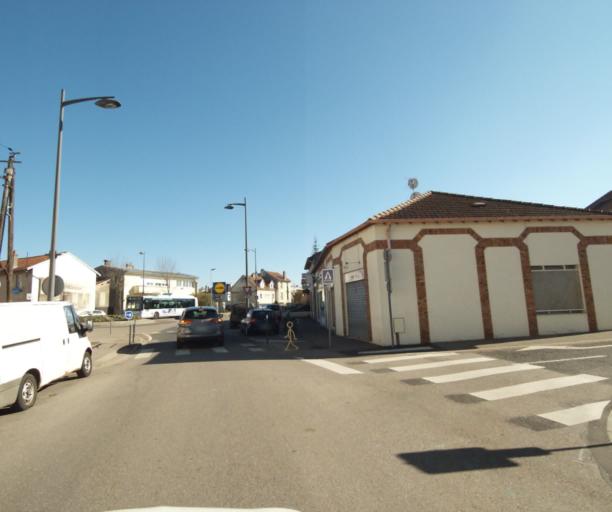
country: FR
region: Lorraine
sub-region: Departement de Meurthe-et-Moselle
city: Tomblaine
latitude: 48.6845
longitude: 6.2136
